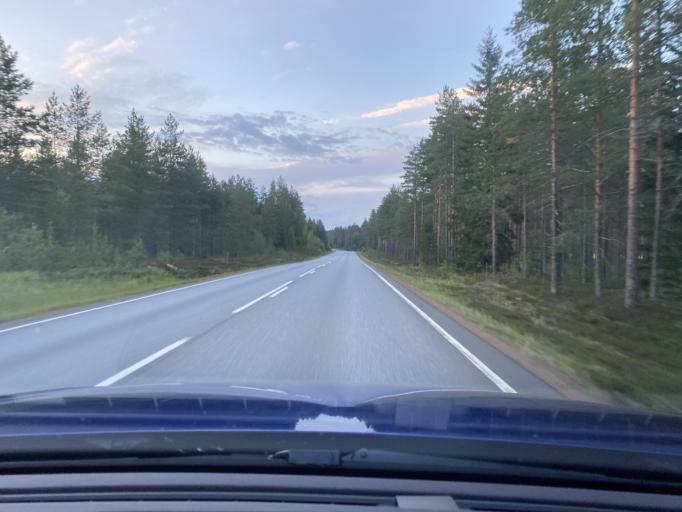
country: FI
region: Satakunta
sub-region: Pohjois-Satakunta
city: Honkajoki
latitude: 62.0342
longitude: 22.2383
